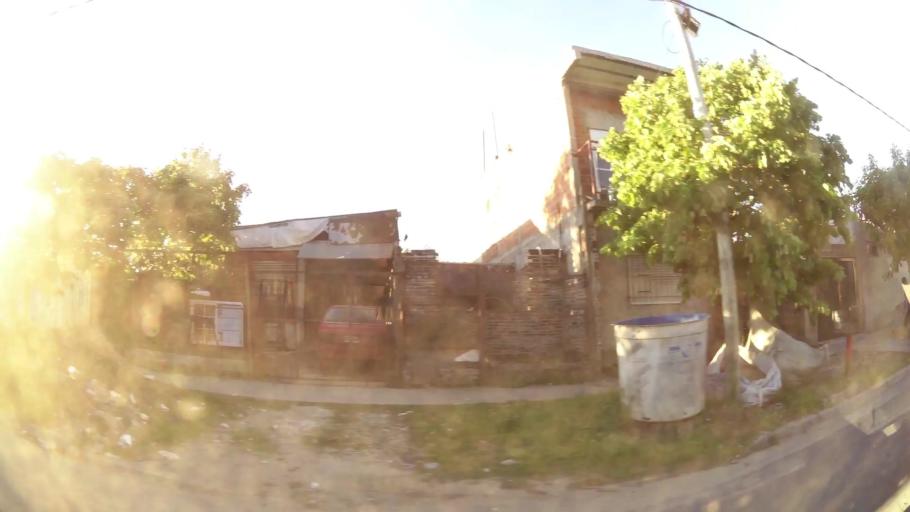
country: AR
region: Buenos Aires
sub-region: Partido de Almirante Brown
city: Adrogue
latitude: -34.7774
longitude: -58.3360
